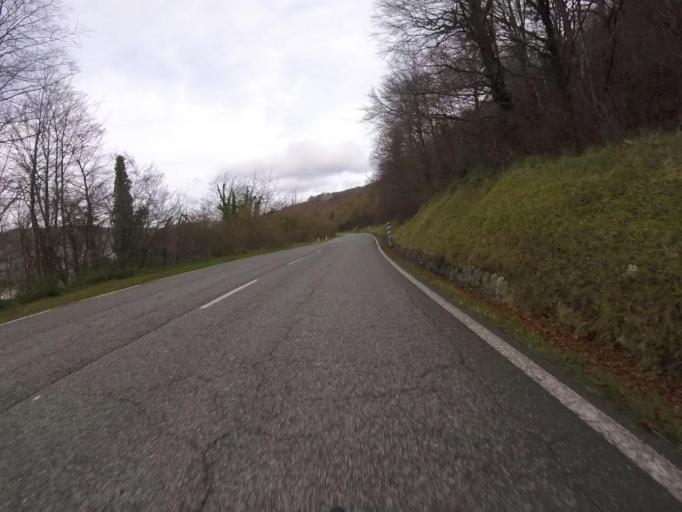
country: ES
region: Navarre
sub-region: Provincia de Navarra
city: Olazagutia
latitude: 42.8634
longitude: -2.1852
